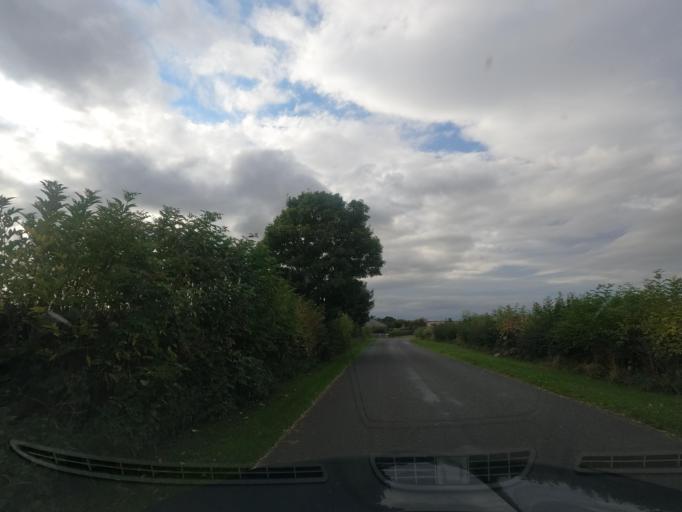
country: GB
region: England
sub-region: Northumberland
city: Ancroft
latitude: 55.6688
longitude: -2.0053
